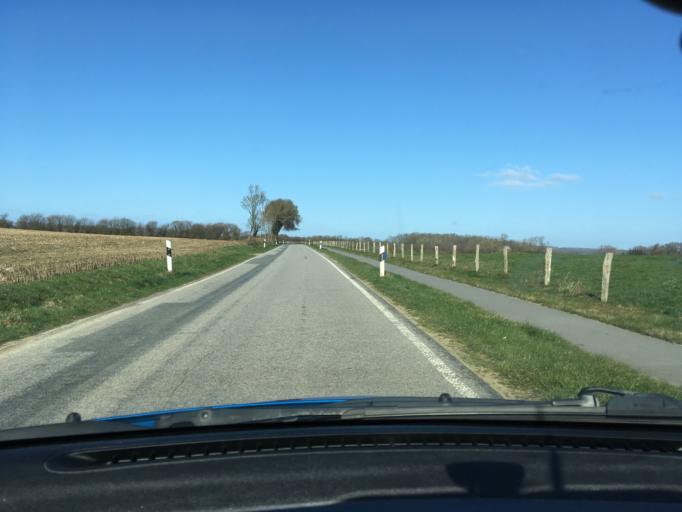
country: DE
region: Schleswig-Holstein
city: Borgwedel
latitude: 54.5002
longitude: 9.6462
